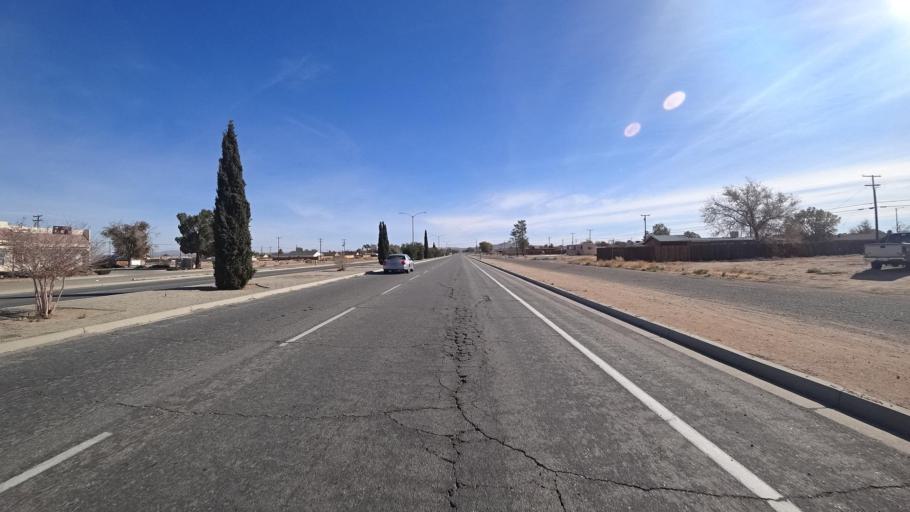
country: US
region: California
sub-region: Kern County
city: California City
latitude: 35.1257
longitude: -117.9719
